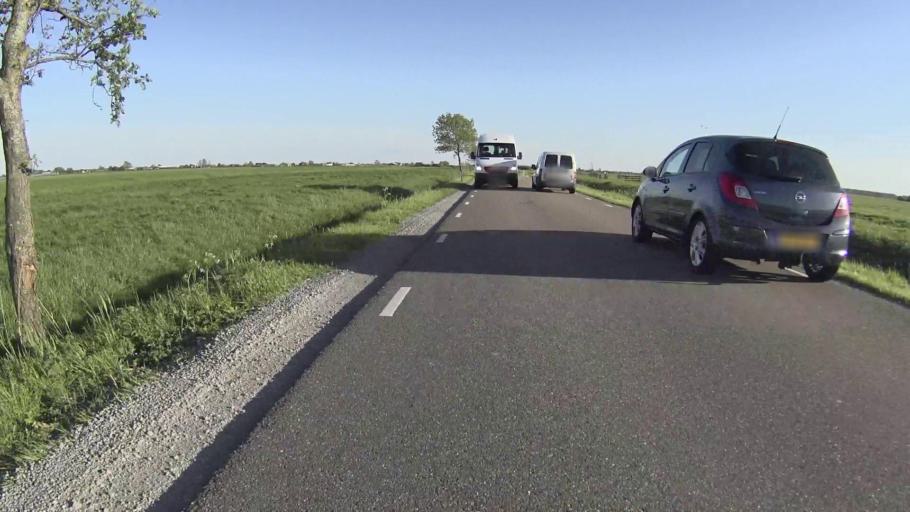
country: NL
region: South Holland
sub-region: Gemeente Rijnwoude
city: Benthuizen
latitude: 52.1147
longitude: 4.5357
